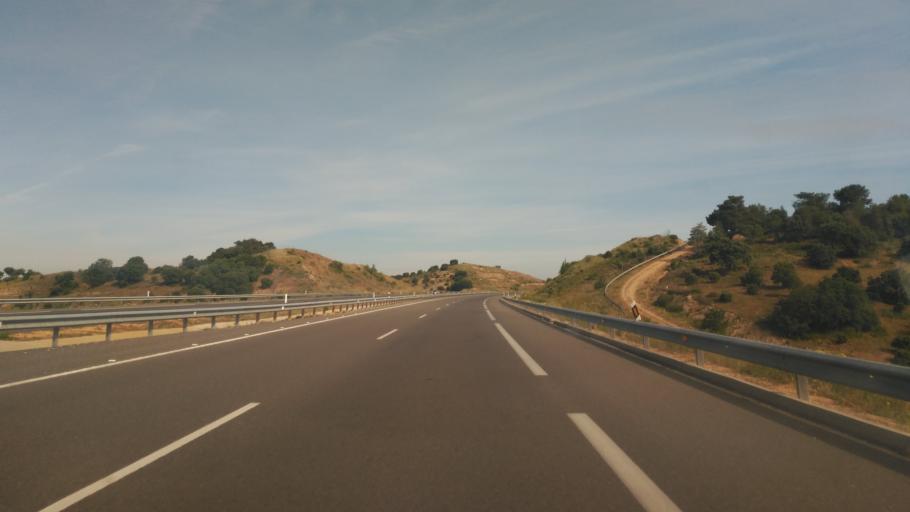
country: ES
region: Castille and Leon
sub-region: Provincia de Zamora
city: Corrales
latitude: 41.3154
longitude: -5.7191
